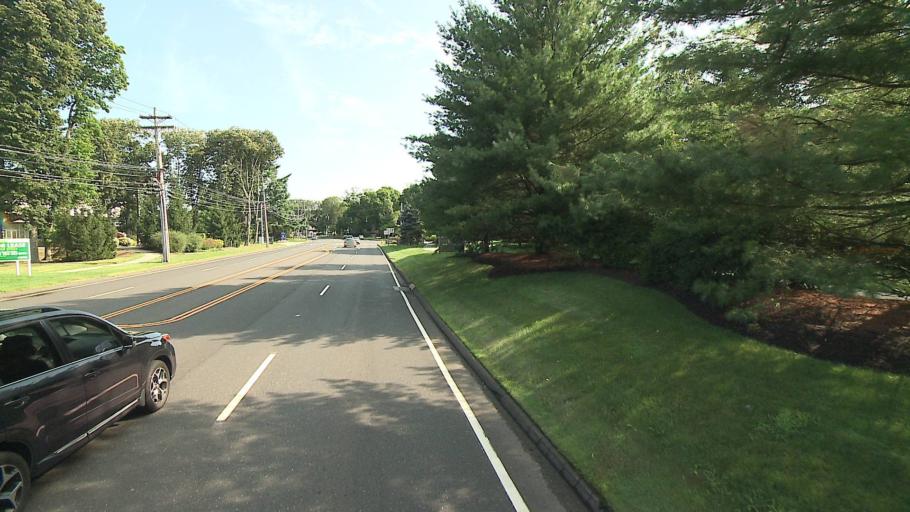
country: US
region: Connecticut
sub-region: Fairfield County
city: Wilton
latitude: 41.1674
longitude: -73.4168
